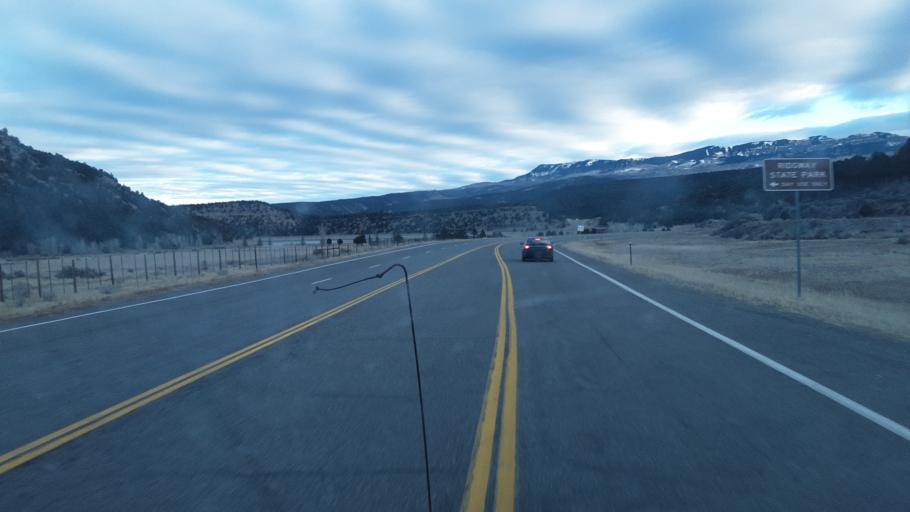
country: US
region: Colorado
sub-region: Ouray County
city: Ouray
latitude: 38.1954
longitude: -107.7431
